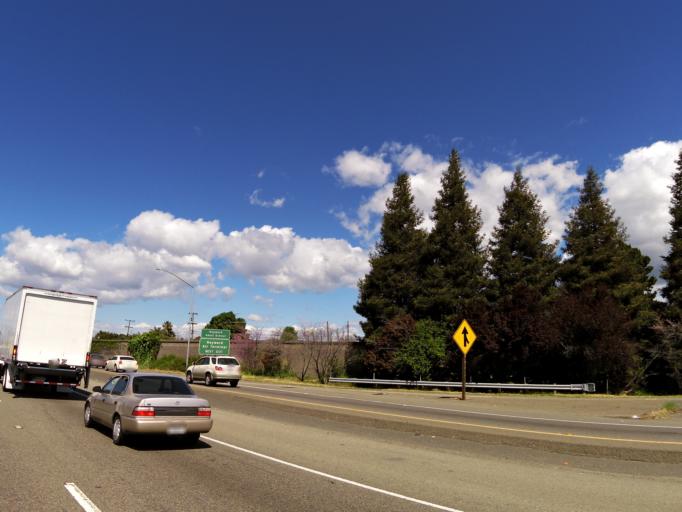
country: US
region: California
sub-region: Alameda County
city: Cherryland
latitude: 37.6578
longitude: -122.1022
